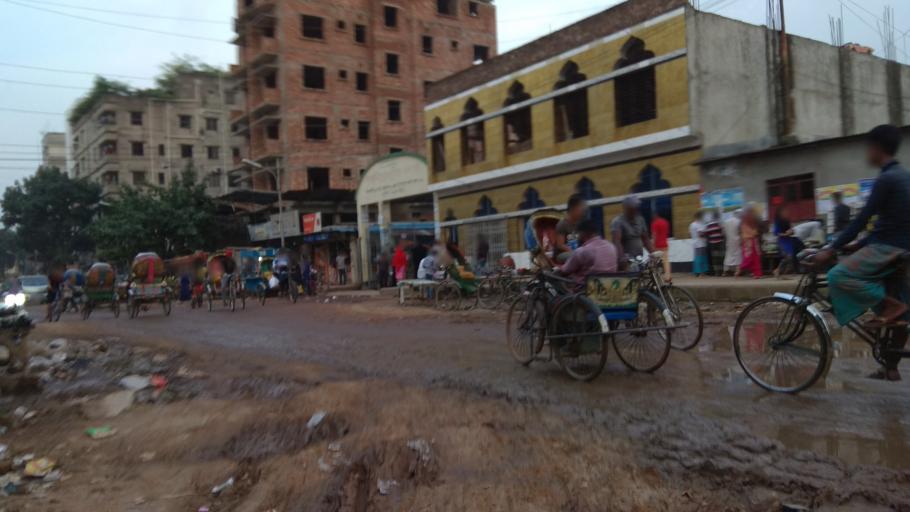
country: BD
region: Dhaka
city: Tungi
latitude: 23.8184
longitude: 90.3761
